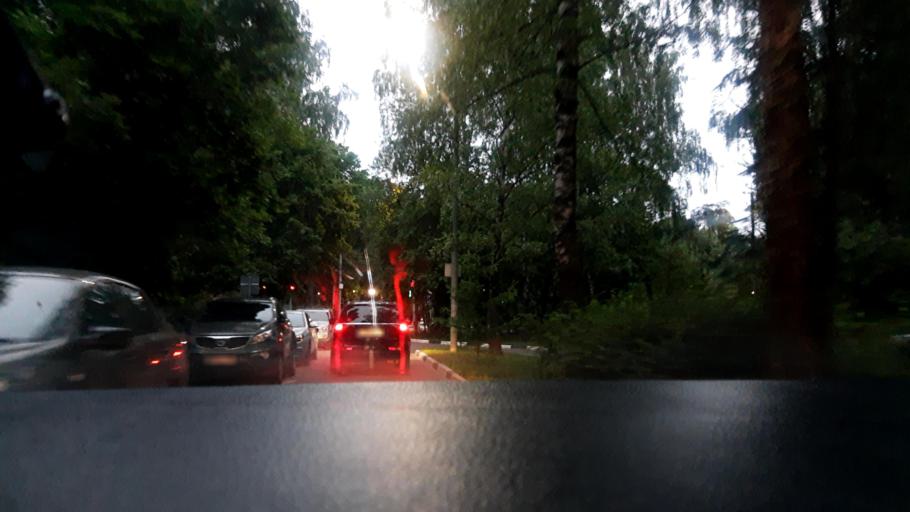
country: RU
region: Moskovskaya
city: Barvikha
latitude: 55.7226
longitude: 37.2763
